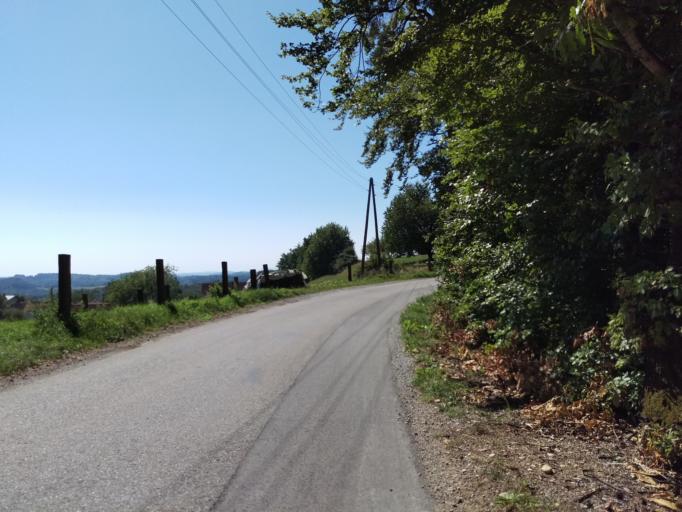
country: AT
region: Styria
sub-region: Politischer Bezirk Graz-Umgebung
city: Eggersdorf bei Graz
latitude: 47.0814
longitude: 15.5587
